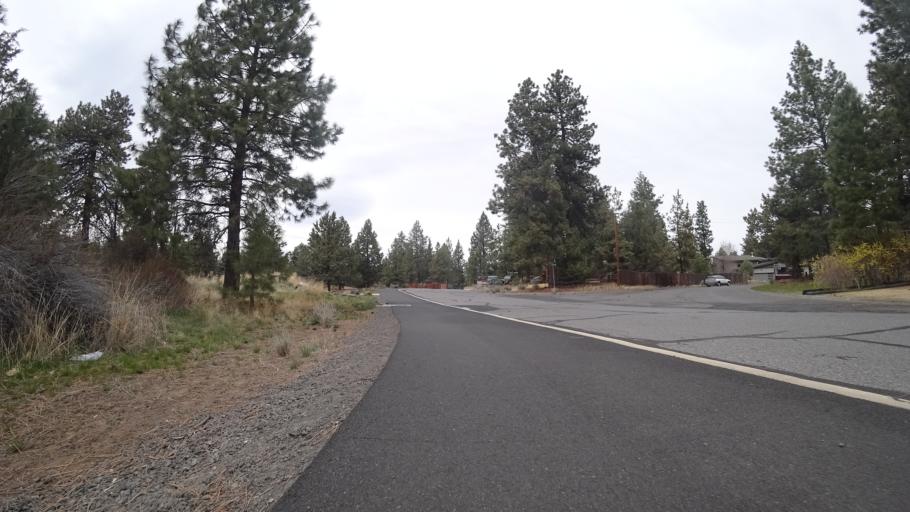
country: US
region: Oregon
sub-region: Deschutes County
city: Bend
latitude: 44.0541
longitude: -121.2930
